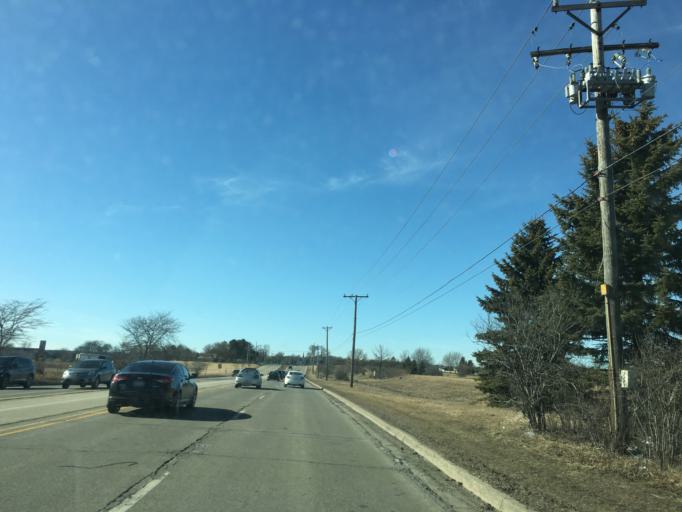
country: US
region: Illinois
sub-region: Cook County
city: Hoffman Estates
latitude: 42.0754
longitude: -88.0661
